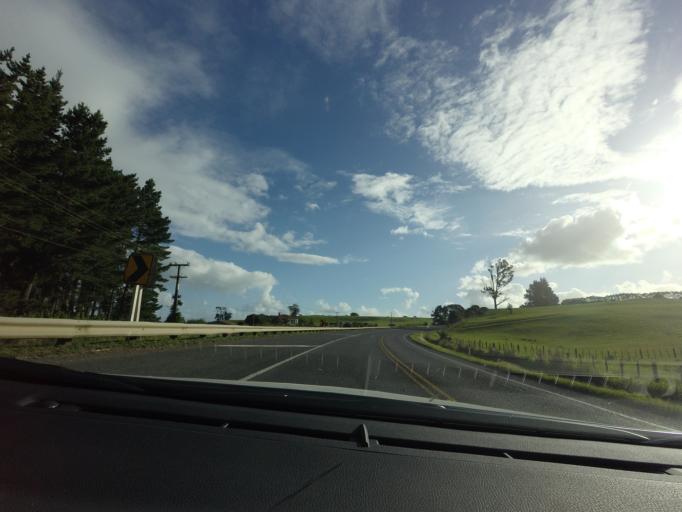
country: NZ
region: Auckland
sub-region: Auckland
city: Pukekohe East
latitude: -37.2221
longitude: 175.0449
